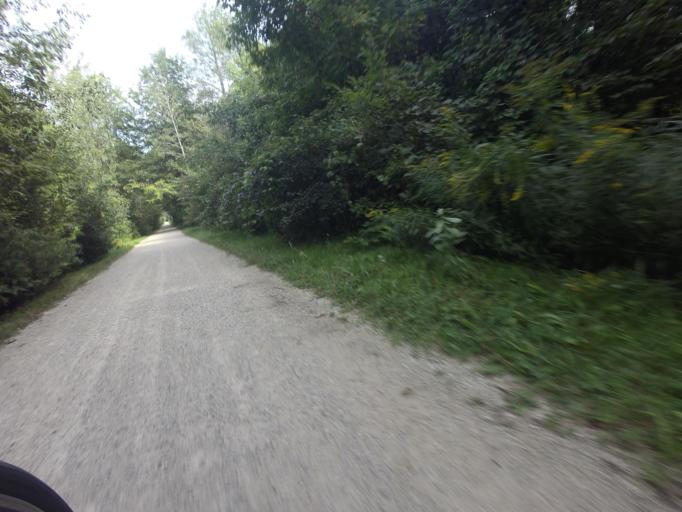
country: CA
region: Ontario
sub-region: Wellington County
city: Guelph
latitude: 43.5698
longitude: -80.3344
